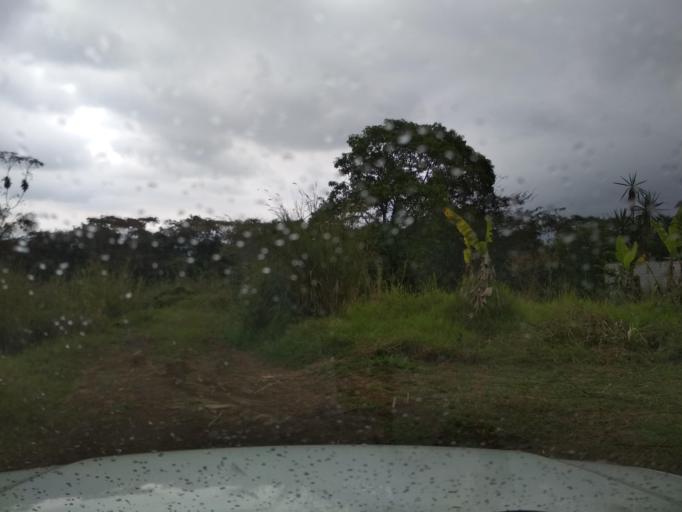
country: MX
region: Veracruz
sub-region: Cordoba
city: Veinte de Noviembre
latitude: 18.8731
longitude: -96.9535
